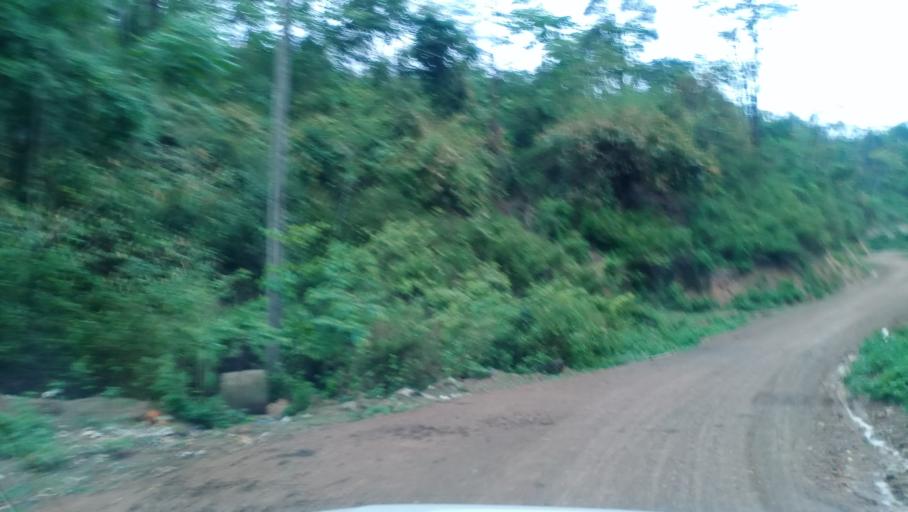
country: LA
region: Phongsali
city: Khoa
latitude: 21.2967
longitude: 102.6987
